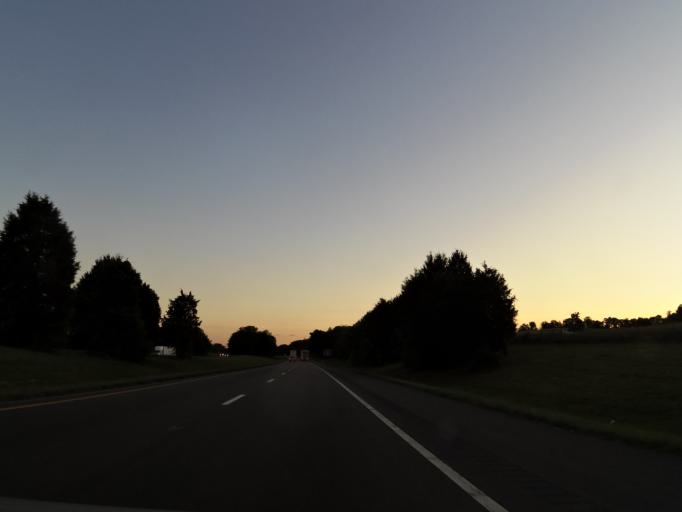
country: US
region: Tennessee
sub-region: Jefferson County
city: White Pine
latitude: 36.1260
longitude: -83.3174
